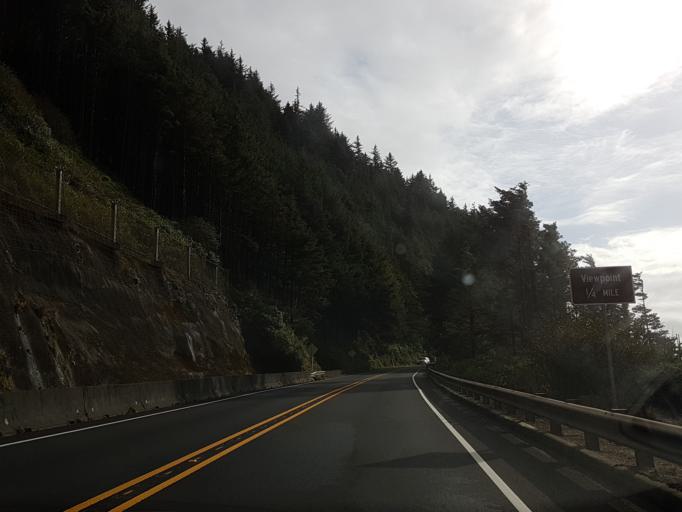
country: US
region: Oregon
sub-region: Lane County
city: Florence
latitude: 44.1285
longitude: -124.1229
